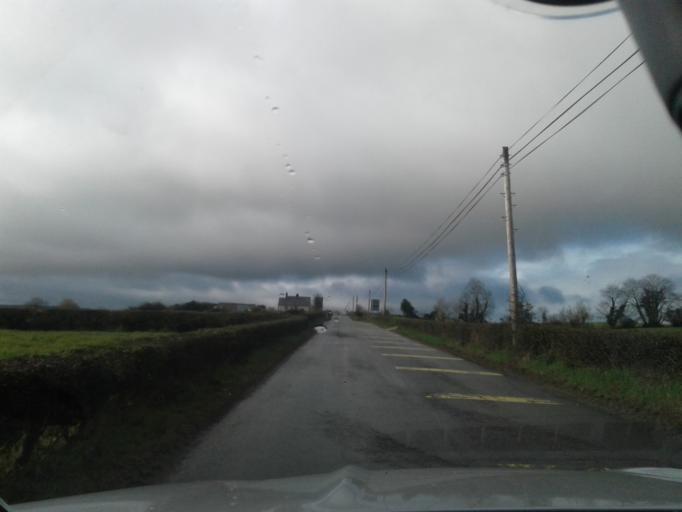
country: IE
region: Ulster
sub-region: County Donegal
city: Ramelton
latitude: 55.0542
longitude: -7.6375
